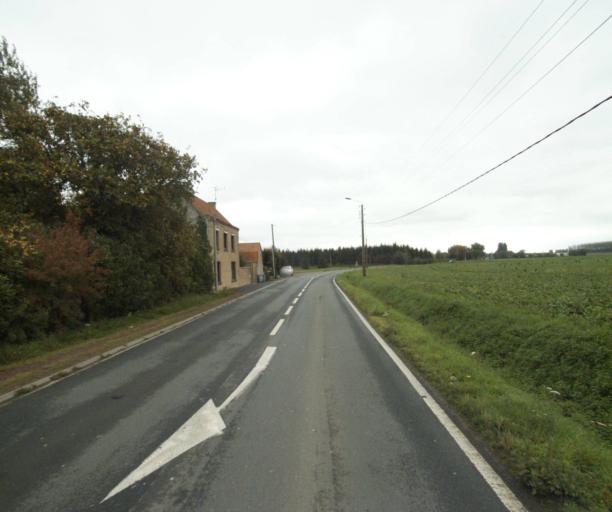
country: FR
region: Nord-Pas-de-Calais
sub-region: Departement du Nord
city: Wavrin
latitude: 50.5853
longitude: 2.9306
